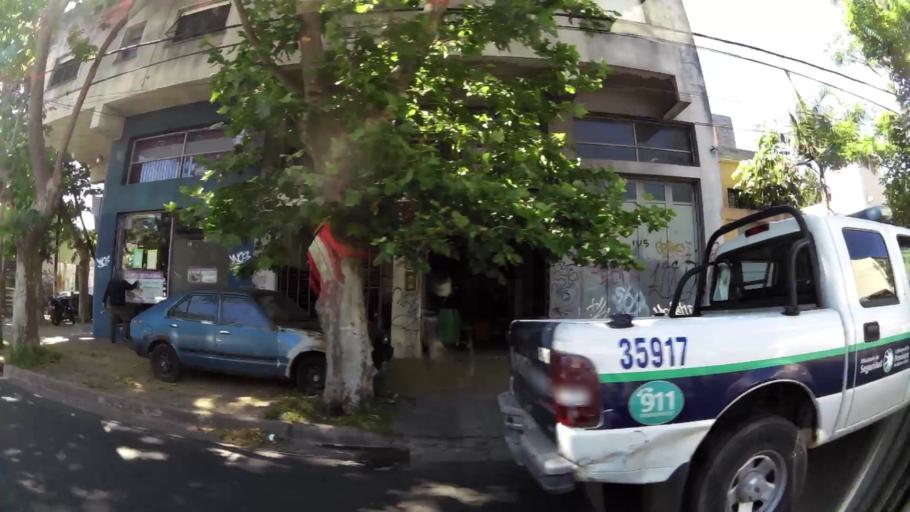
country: AR
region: Buenos Aires
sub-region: Partido de Vicente Lopez
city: Olivos
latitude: -34.5290
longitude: -58.5016
